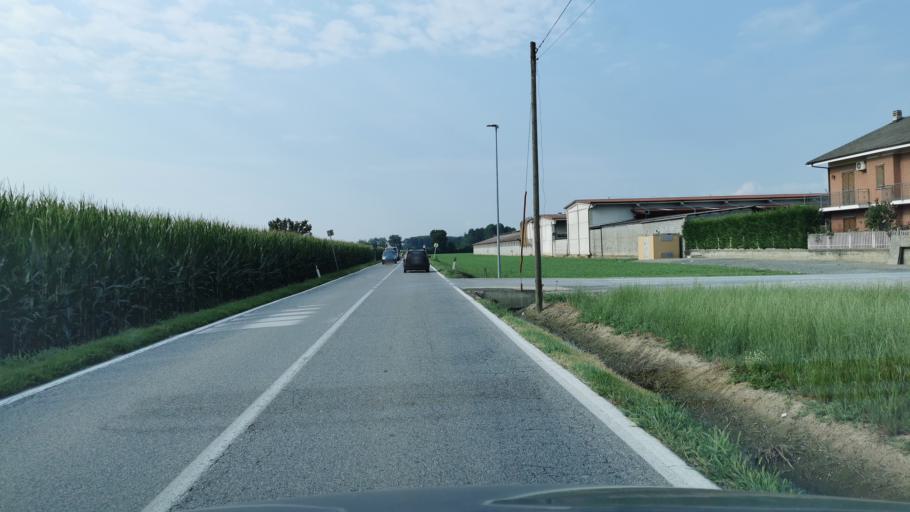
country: IT
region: Piedmont
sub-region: Provincia di Torino
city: Scalenghe
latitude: 44.8797
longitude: 7.4945
